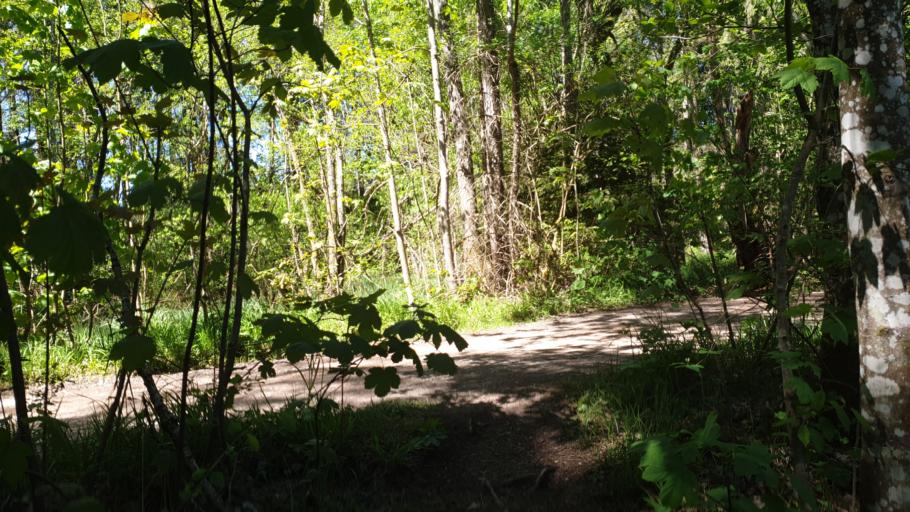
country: DE
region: Bavaria
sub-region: Upper Bavaria
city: Iffeldorf
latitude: 47.7841
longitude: 11.2995
